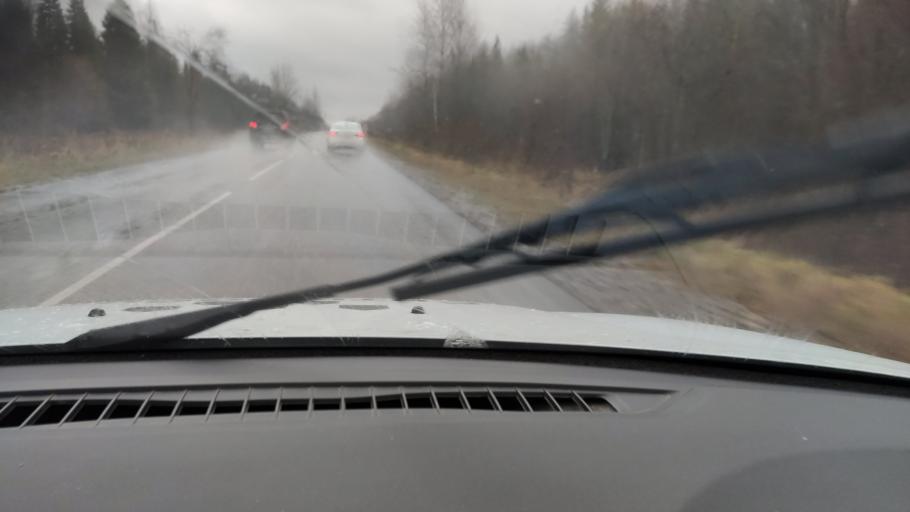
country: RU
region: Perm
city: Novyye Lyady
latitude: 58.0344
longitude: 56.6068
